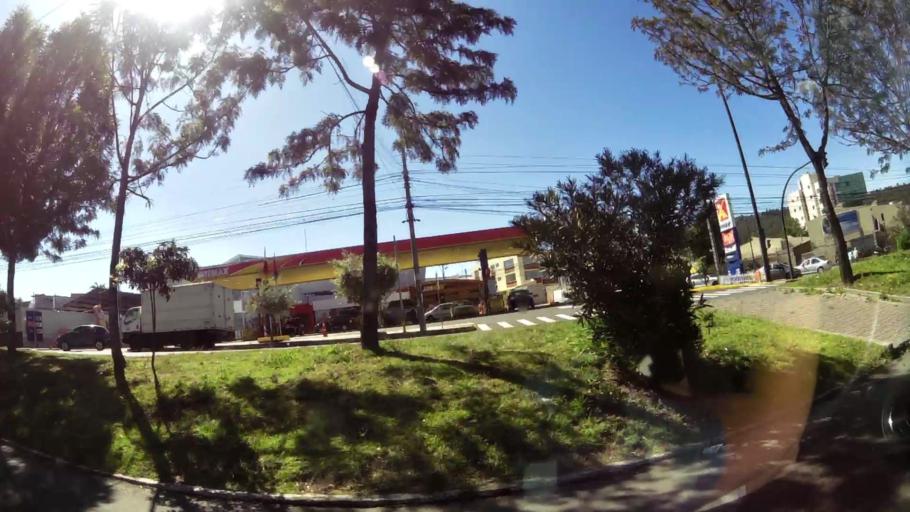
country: EC
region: Pichincha
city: Quito
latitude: -0.1601
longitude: -78.4669
